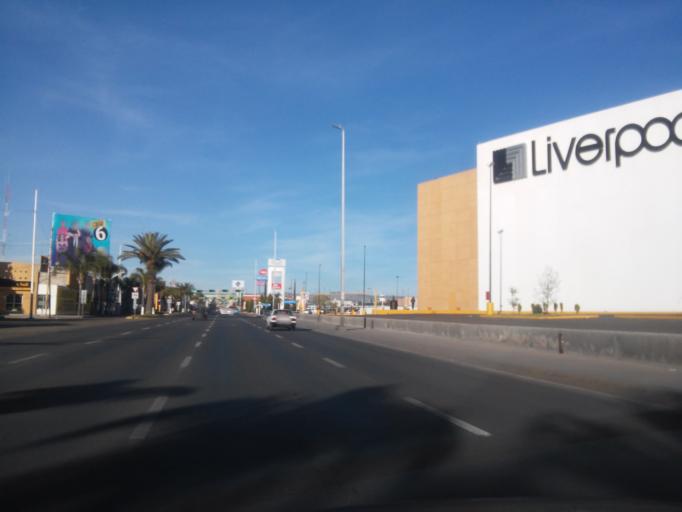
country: MX
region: Durango
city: Victoria de Durango
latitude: 24.0345
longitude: -104.6495
